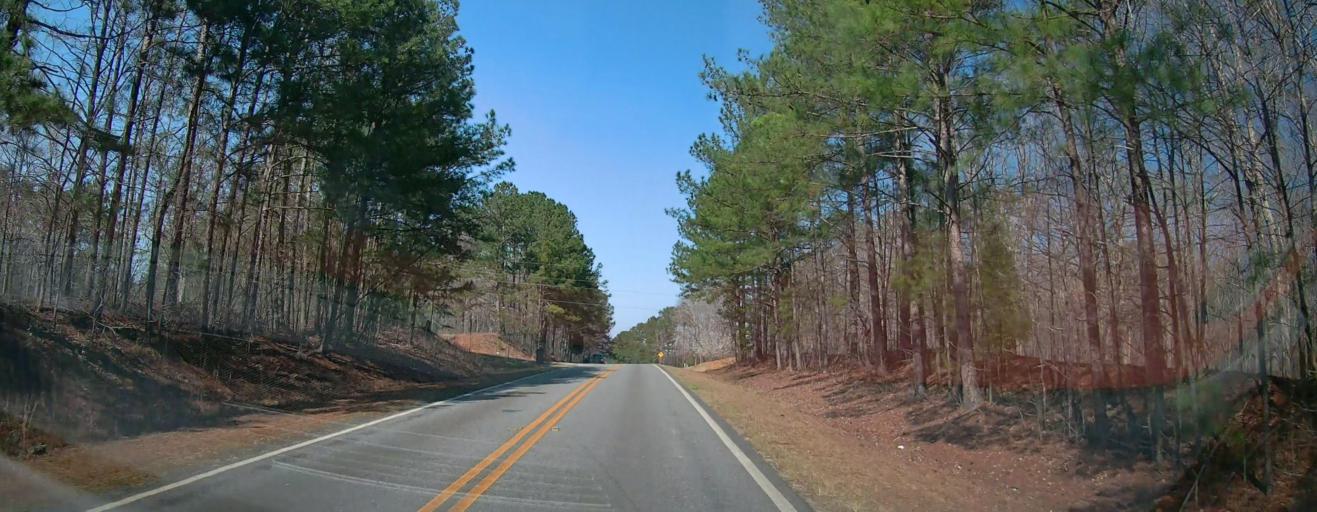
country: US
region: Georgia
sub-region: Jones County
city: Gray
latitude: 32.9523
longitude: -83.5439
